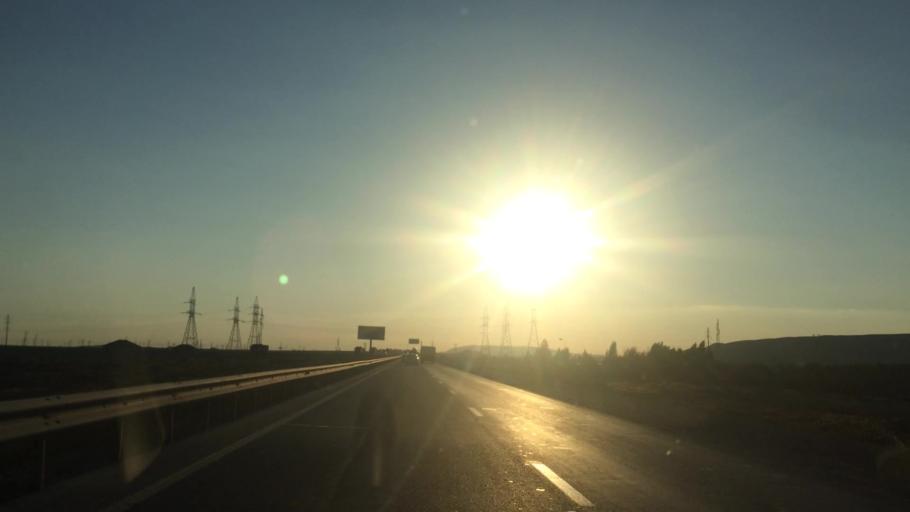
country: AZ
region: Baki
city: Qobustan
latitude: 39.9639
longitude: 49.4015
